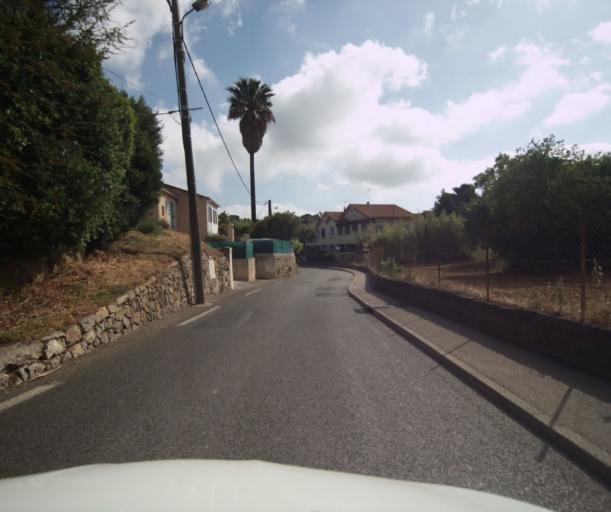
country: FR
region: Provence-Alpes-Cote d'Azur
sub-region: Departement du Var
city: La Seyne-sur-Mer
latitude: 43.0969
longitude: 5.8686
